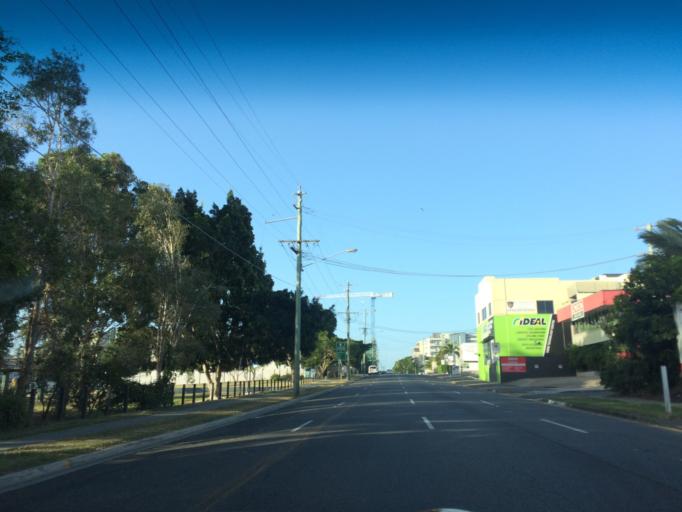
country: AU
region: Queensland
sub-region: Brisbane
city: Woolloongabba
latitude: -27.4814
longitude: 153.0409
